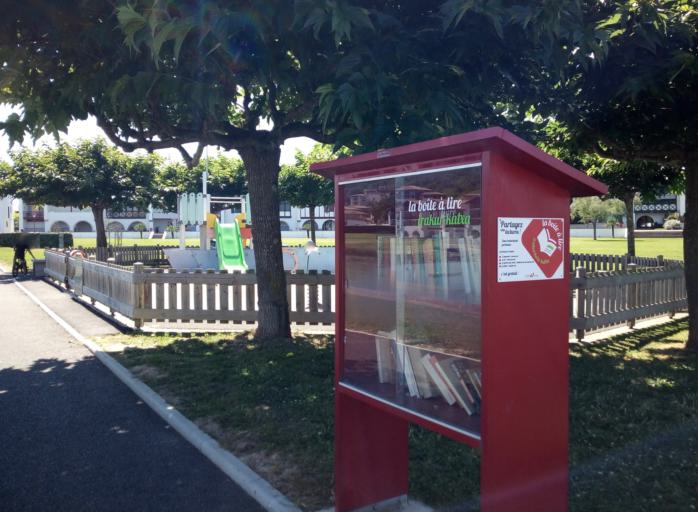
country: FR
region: Aquitaine
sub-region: Departement des Pyrenees-Atlantiques
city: Ciboure
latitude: 43.3882
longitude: -1.6860
